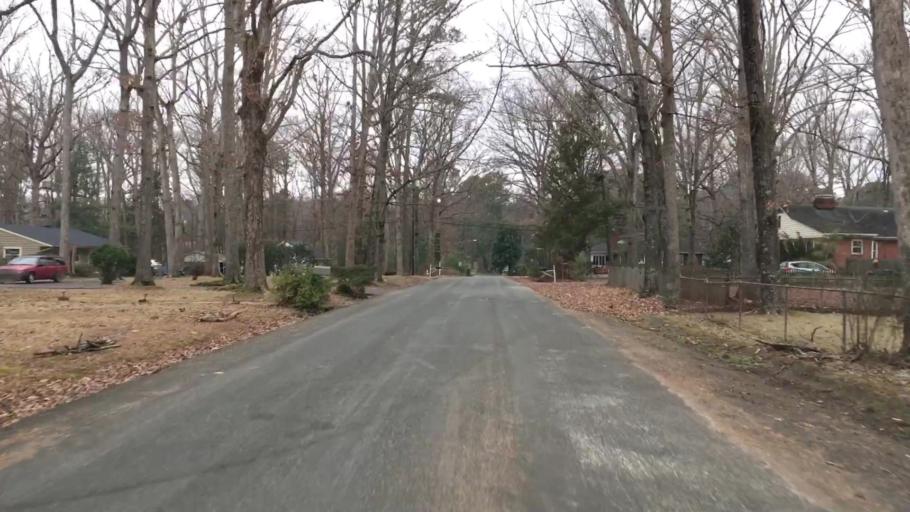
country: US
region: Virginia
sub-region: Chesterfield County
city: Bon Air
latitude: 37.5346
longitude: -77.5748
